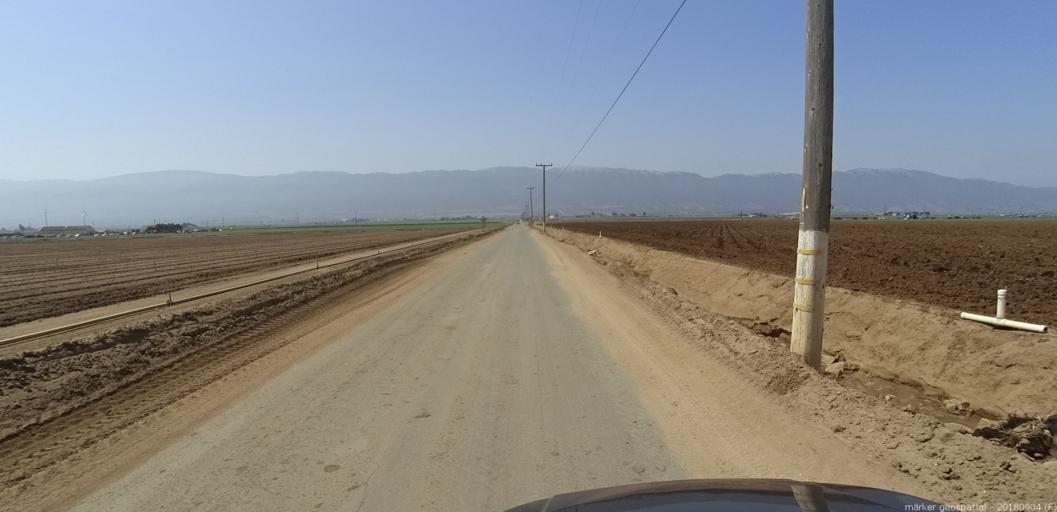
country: US
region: California
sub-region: Monterey County
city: Gonzales
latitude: 36.5310
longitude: -121.4494
